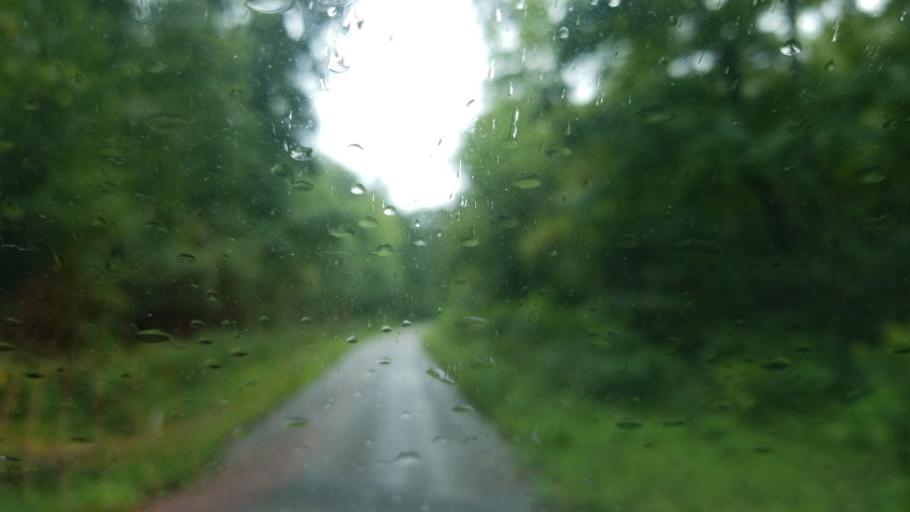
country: US
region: Ohio
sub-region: Scioto County
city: West Portsmouth
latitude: 38.7748
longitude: -83.1520
